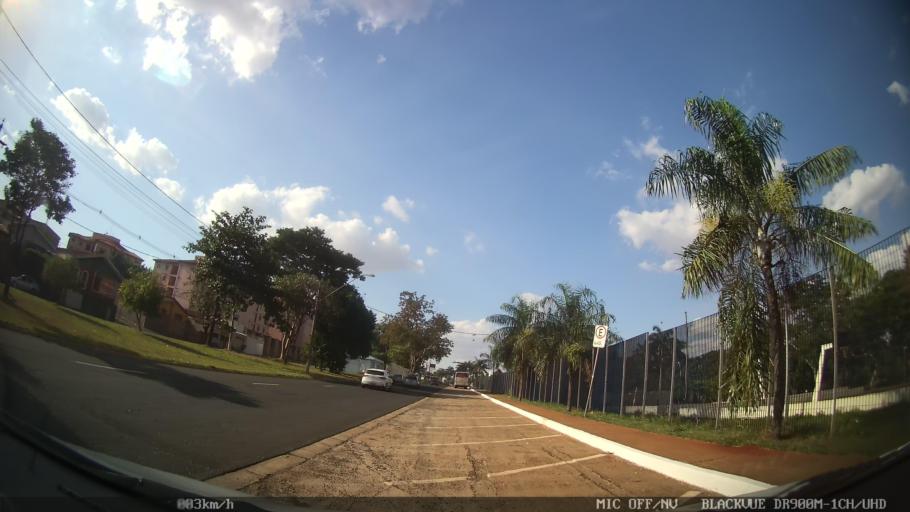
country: BR
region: Sao Paulo
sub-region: Ribeirao Preto
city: Ribeirao Preto
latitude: -21.1761
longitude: -47.8195
